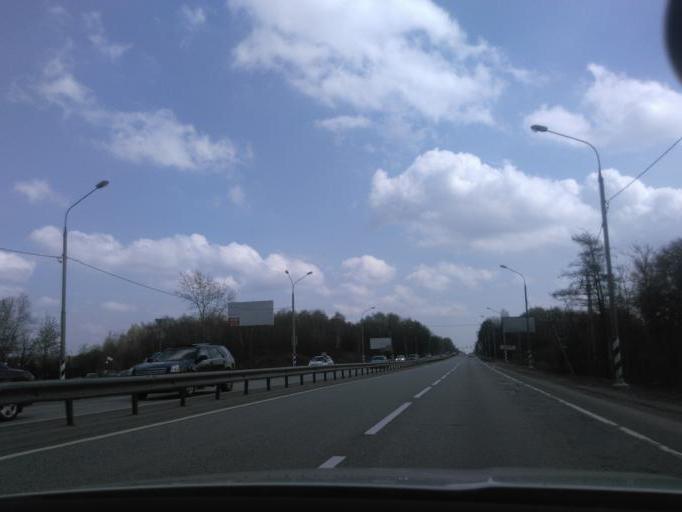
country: RU
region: Moskovskaya
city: Chashnikovo
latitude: 56.0264
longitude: 37.1766
